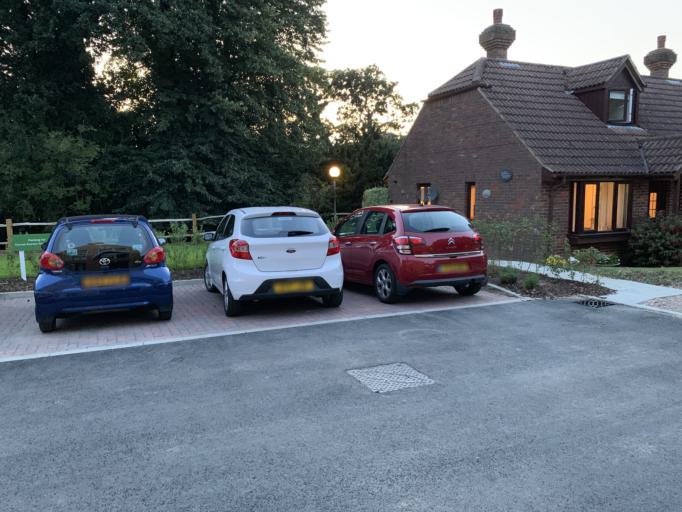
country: GB
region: England
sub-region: East Sussex
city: Uckfield
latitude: 50.9733
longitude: 0.0929
